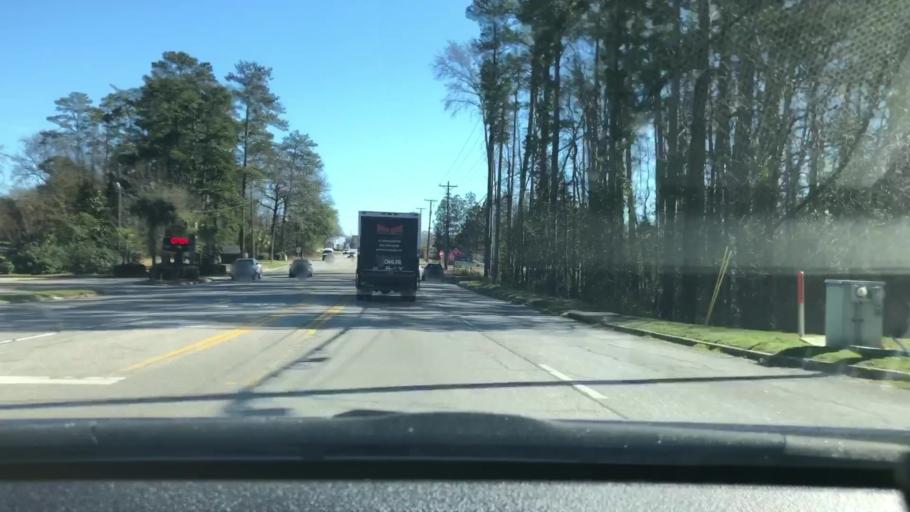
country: US
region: South Carolina
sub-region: Lexington County
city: Oak Grove
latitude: 34.0060
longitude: -81.1205
